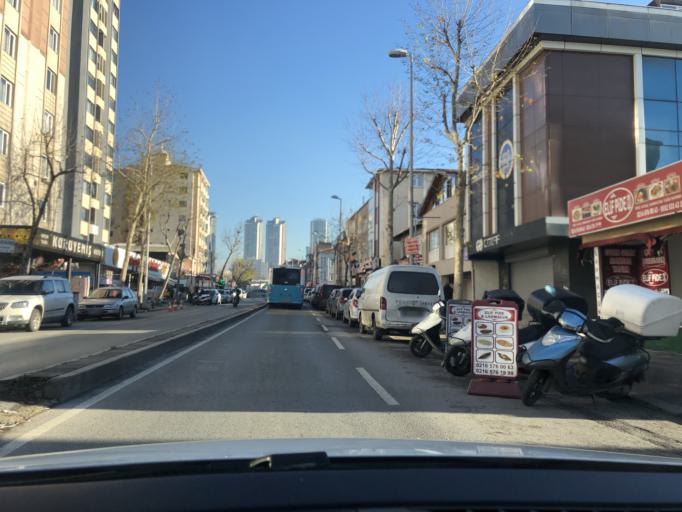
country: TR
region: Istanbul
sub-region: Atasehir
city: Atasehir
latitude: 40.9767
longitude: 29.1238
